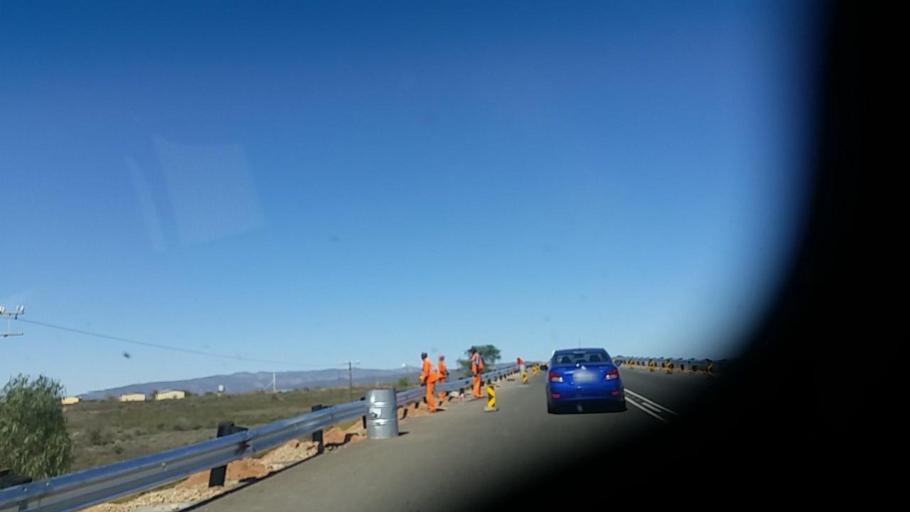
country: ZA
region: Western Cape
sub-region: Eden District Municipality
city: Oudtshoorn
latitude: -33.5847
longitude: 22.2917
